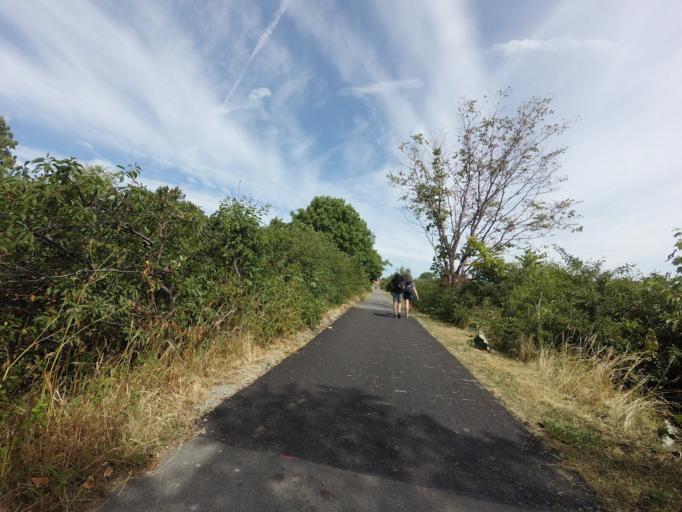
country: SE
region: Skane
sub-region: Simrishamns Kommun
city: Simrishamn
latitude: 55.5410
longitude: 14.3563
